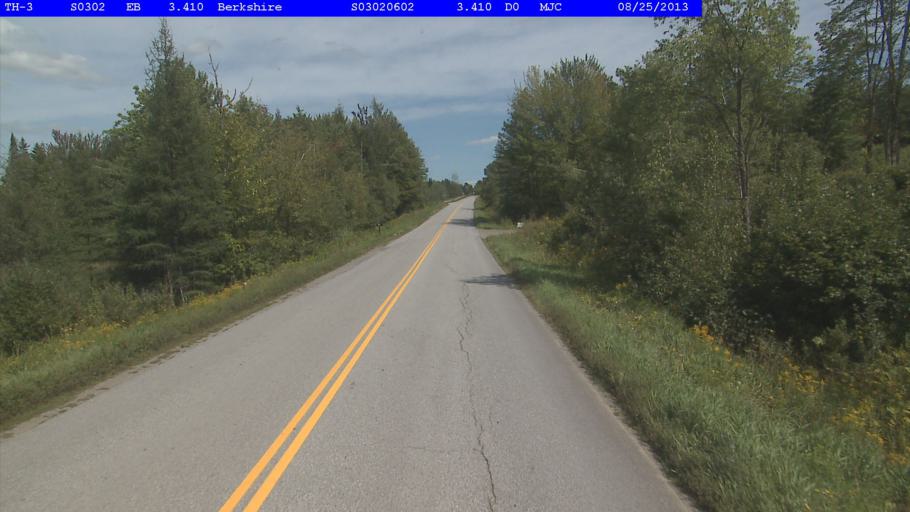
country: US
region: Vermont
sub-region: Franklin County
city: Richford
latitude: 44.9786
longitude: -72.7527
